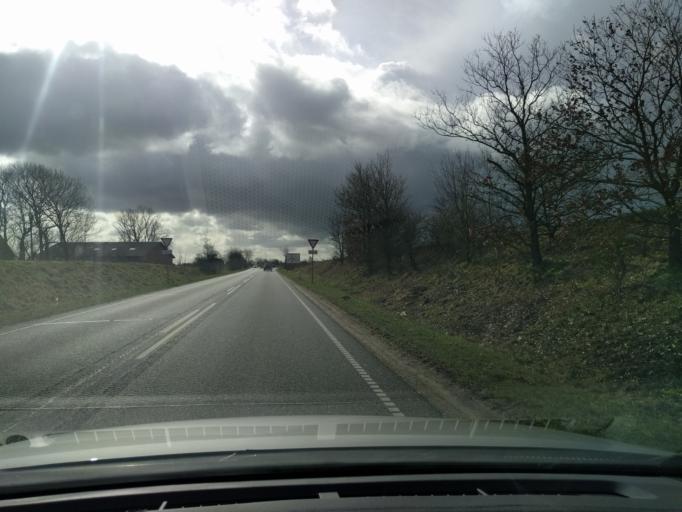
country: DK
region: South Denmark
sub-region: Kolding Kommune
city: Vamdrup
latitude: 55.4298
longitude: 9.3056
